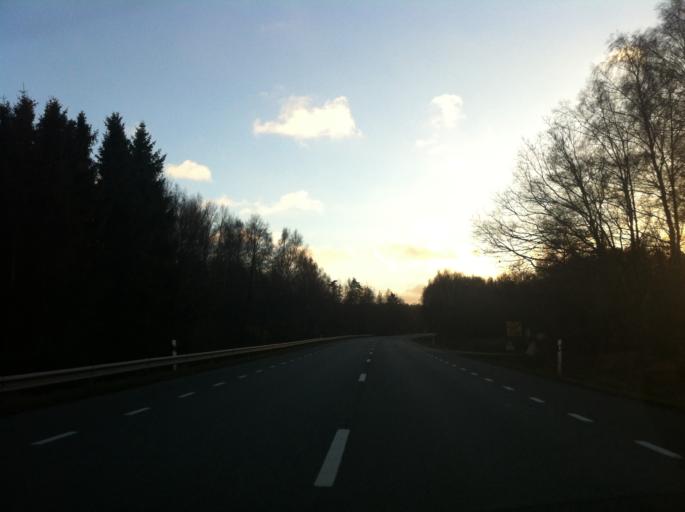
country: SE
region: Skane
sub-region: Hassleholms Kommun
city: Sosdala
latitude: 56.0512
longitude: 13.7182
